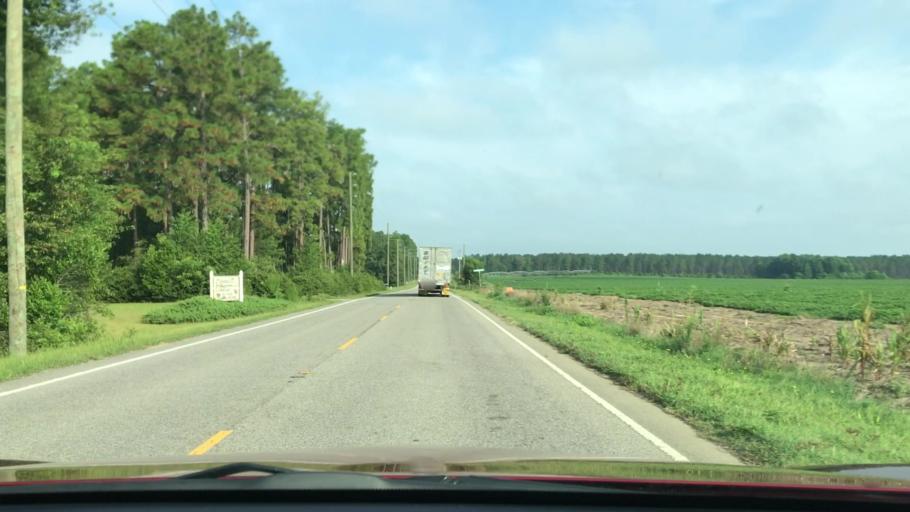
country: US
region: South Carolina
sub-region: Barnwell County
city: Blackville
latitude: 33.6106
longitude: -81.2759
